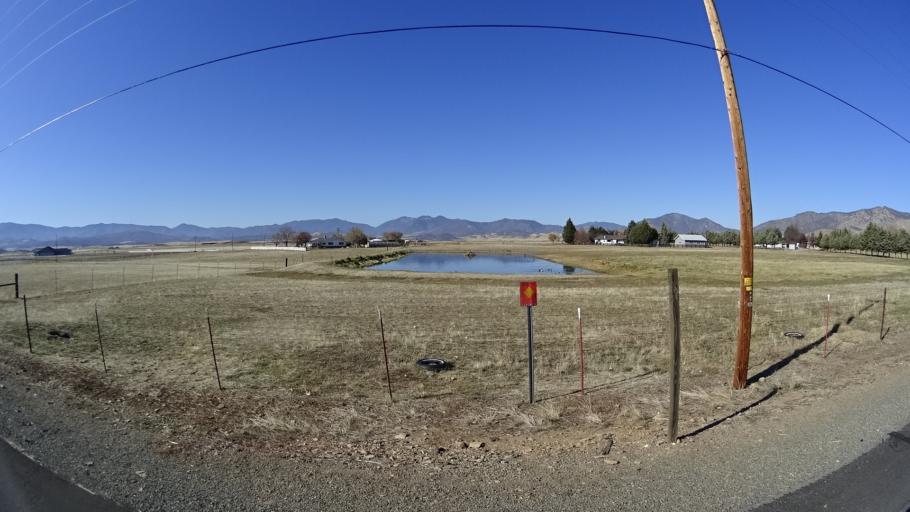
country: US
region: California
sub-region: Siskiyou County
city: Montague
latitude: 41.7507
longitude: -122.5248
